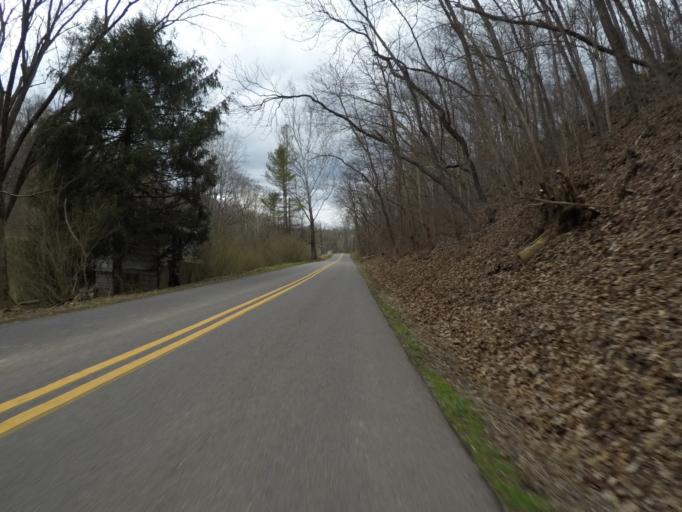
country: US
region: Ohio
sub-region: Lawrence County
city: Burlington
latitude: 38.4534
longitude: -82.5308
